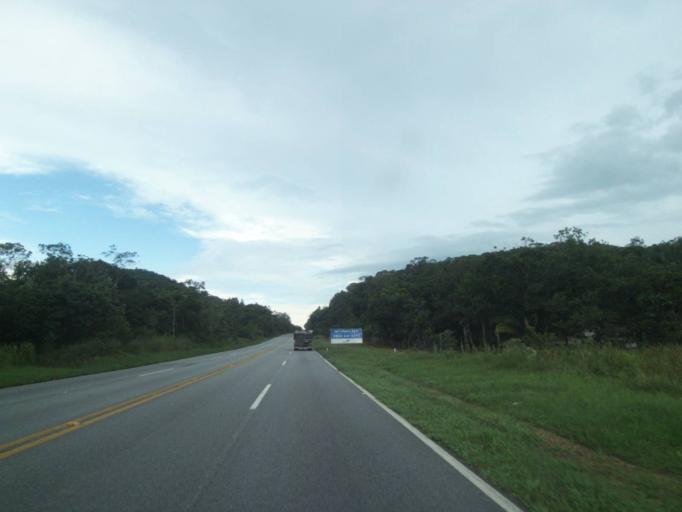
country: BR
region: Parana
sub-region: Pontal Do Parana
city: Pontal do Parana
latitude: -25.6787
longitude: -48.5778
